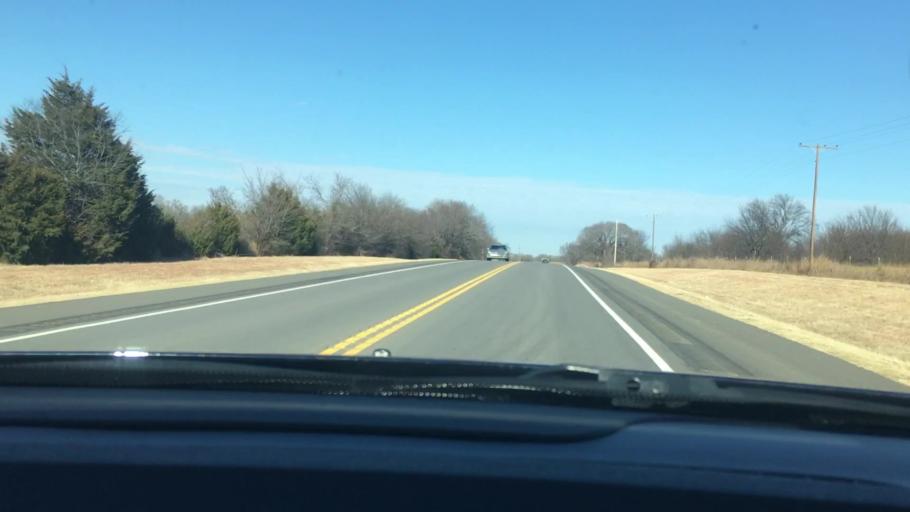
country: US
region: Oklahoma
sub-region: Murray County
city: Davis
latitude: 34.5588
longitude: -97.1341
